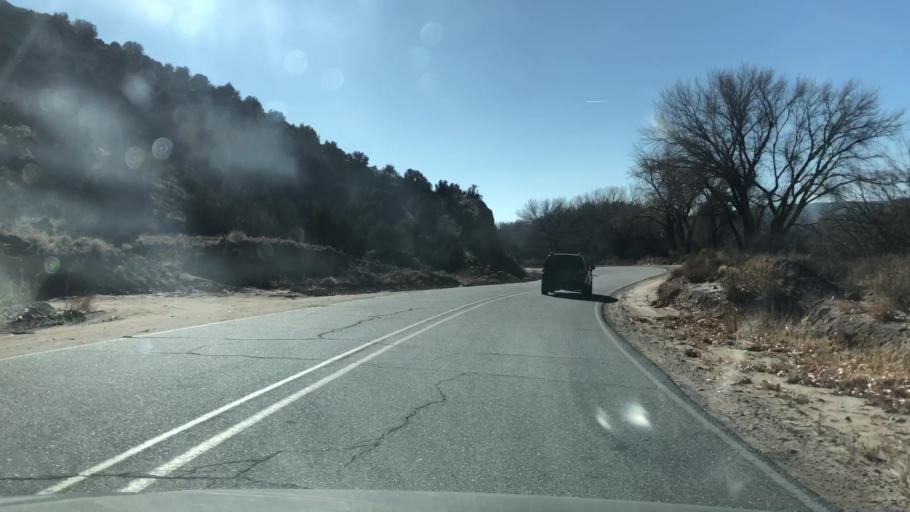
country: US
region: New Mexico
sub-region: Rio Arriba County
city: Ohkay Owingeh
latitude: 36.0910
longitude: -106.1294
